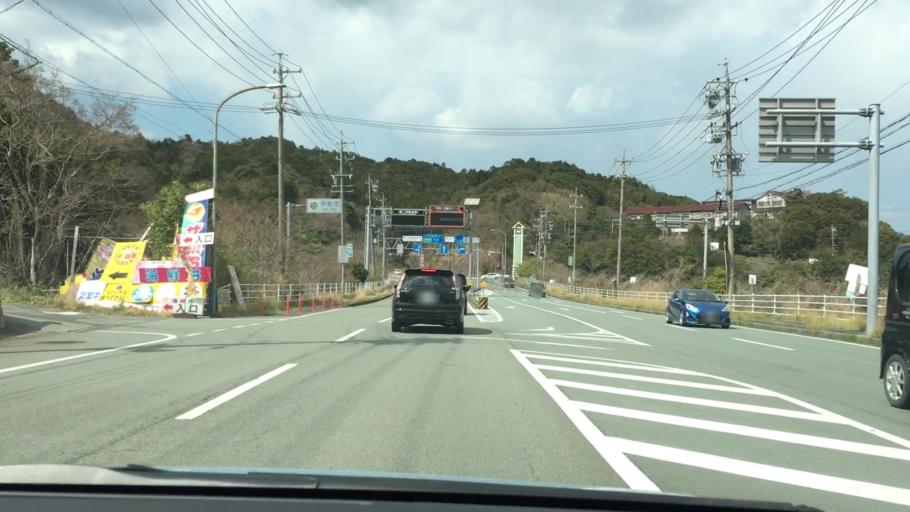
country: JP
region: Mie
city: Toba
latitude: 34.4843
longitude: 136.8160
